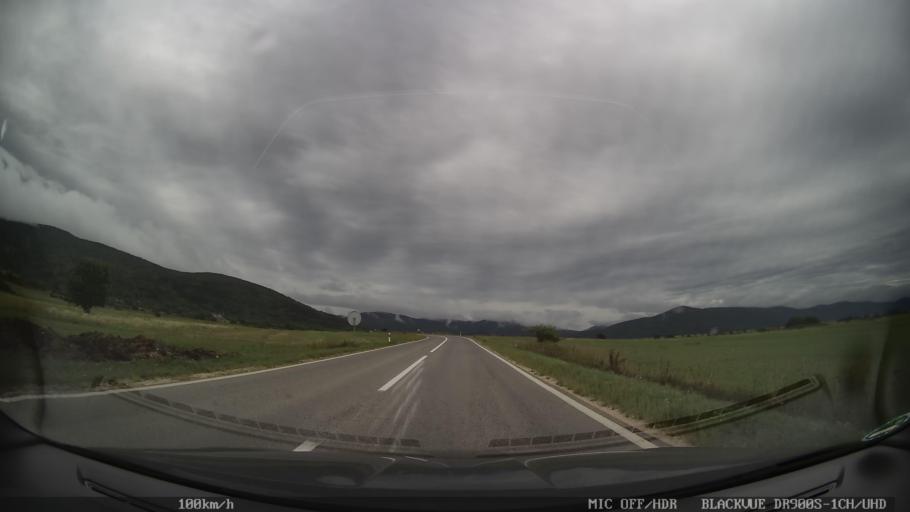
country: HR
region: Licko-Senjska
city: Otocac
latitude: 44.8561
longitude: 15.2849
